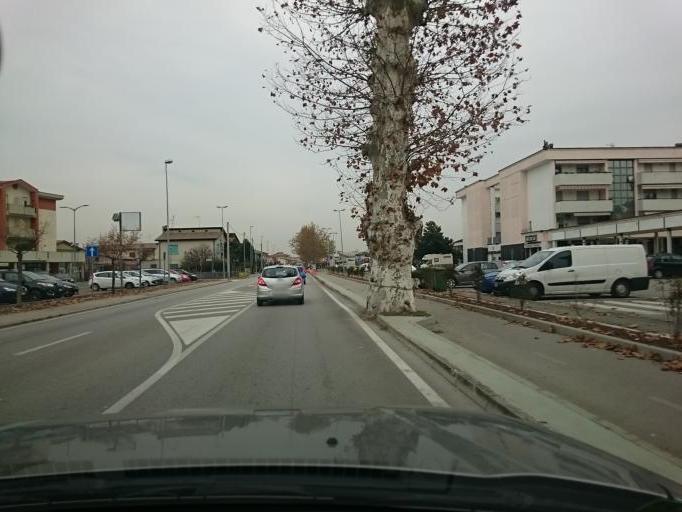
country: IT
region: Veneto
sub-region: Provincia di Padova
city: Masera di Padova
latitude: 45.3158
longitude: 11.8638
